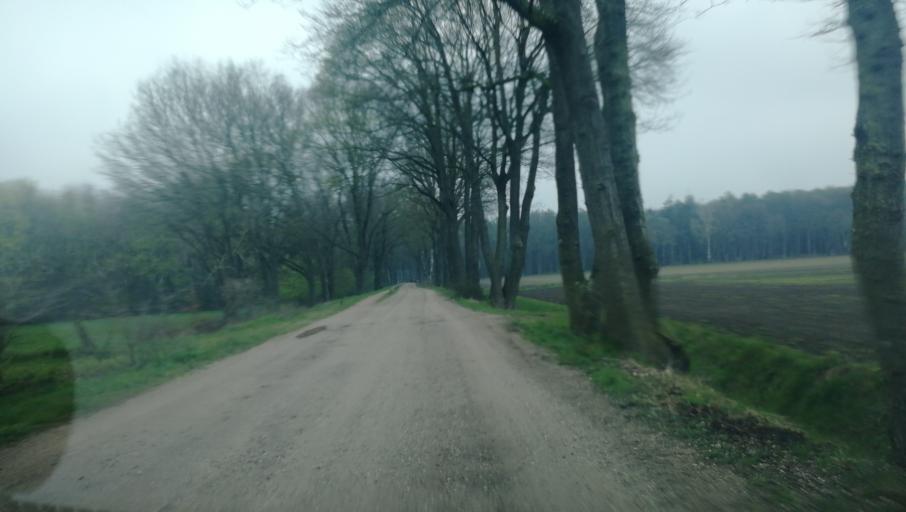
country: NL
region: Limburg
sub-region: Gemeente Beesel
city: Beesel
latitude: 51.2929
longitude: 6.0045
